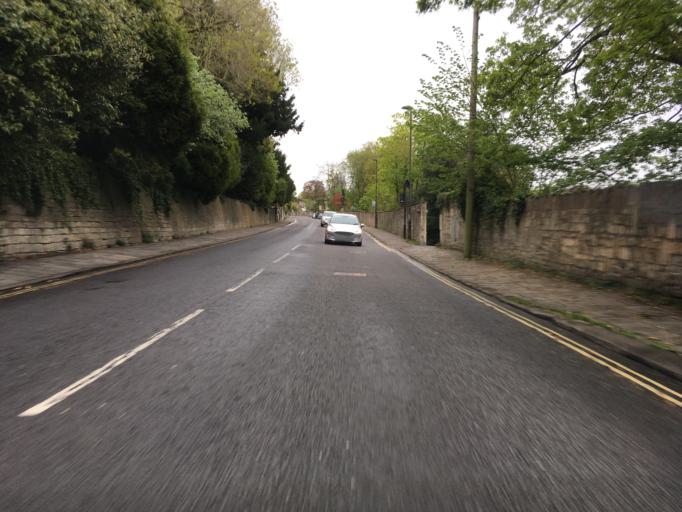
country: GB
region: England
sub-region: Bath and North East Somerset
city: Bath
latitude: 51.3779
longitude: -2.3386
